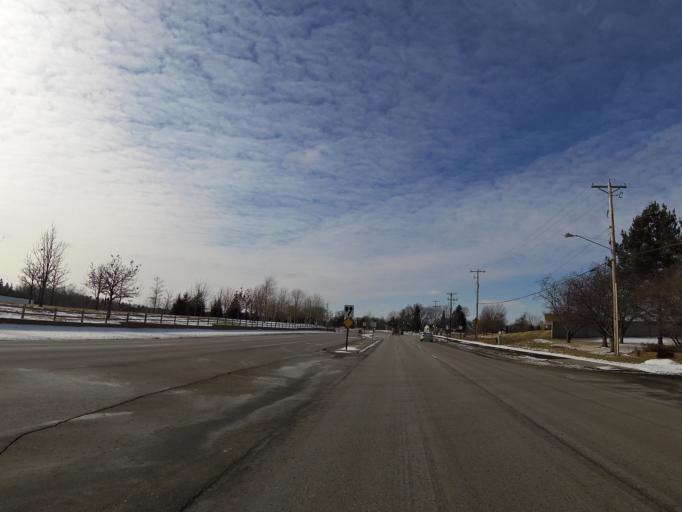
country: US
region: Minnesota
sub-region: Hennepin County
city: Eden Prairie
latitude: 44.8376
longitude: -93.4770
